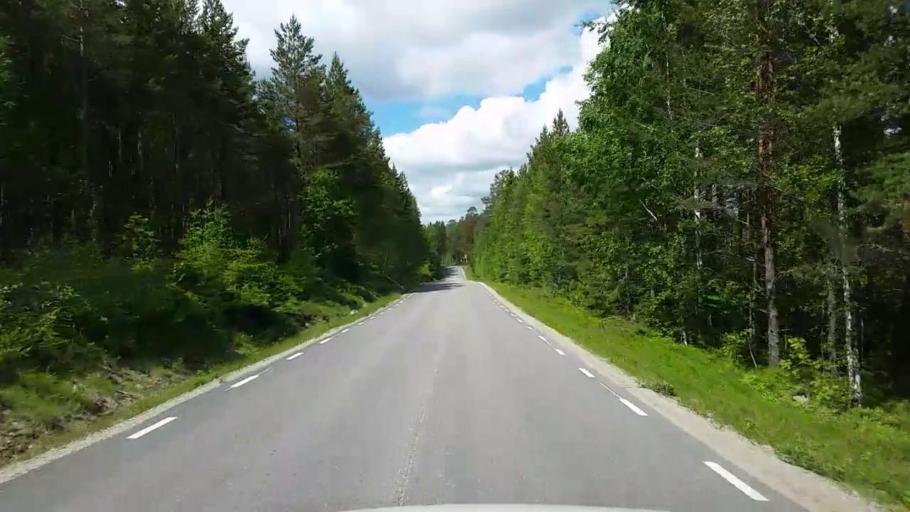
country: SE
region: Gaevleborg
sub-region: Bollnas Kommun
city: Vittsjo
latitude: 61.1058
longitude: 16.1587
